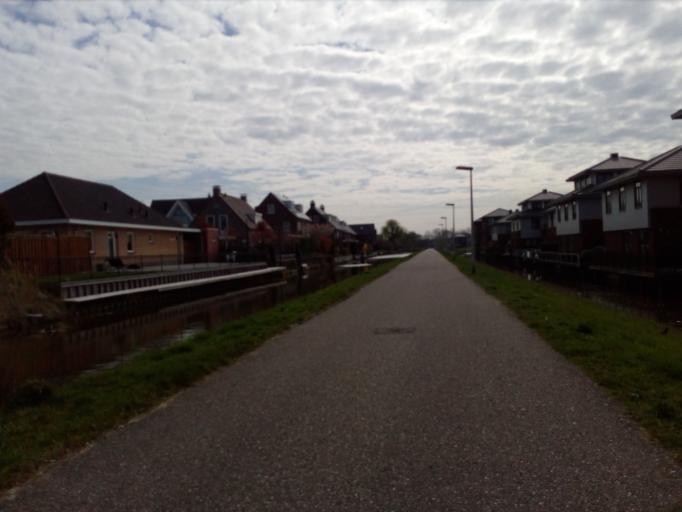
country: NL
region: South Holland
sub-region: Gemeente Den Haag
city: Ypenburg
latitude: 52.0422
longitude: 4.3768
